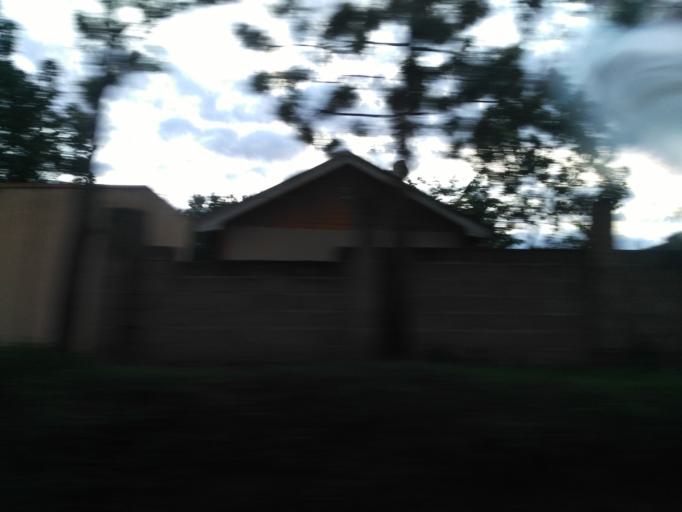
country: UG
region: Eastern Region
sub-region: Jinja District
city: Jinja
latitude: 0.4439
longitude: 33.2030
